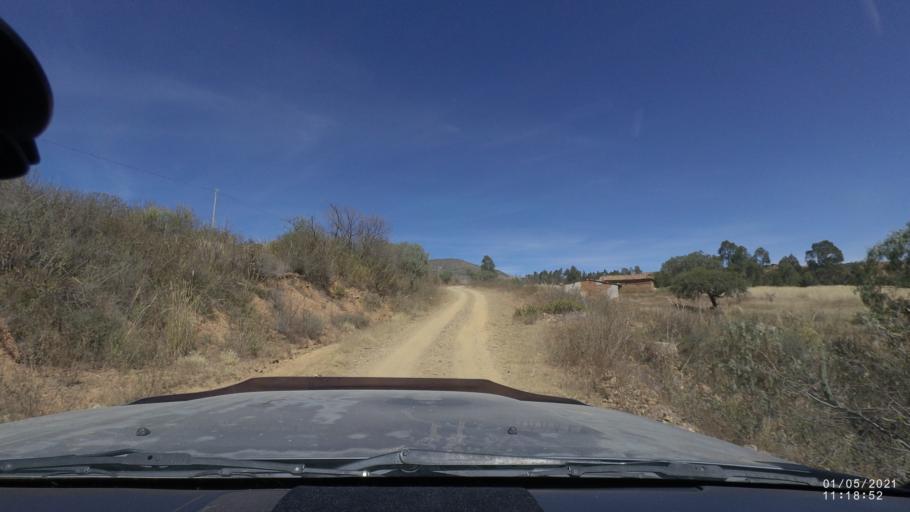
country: BO
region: Cochabamba
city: Tarata
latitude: -17.6416
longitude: -66.1188
